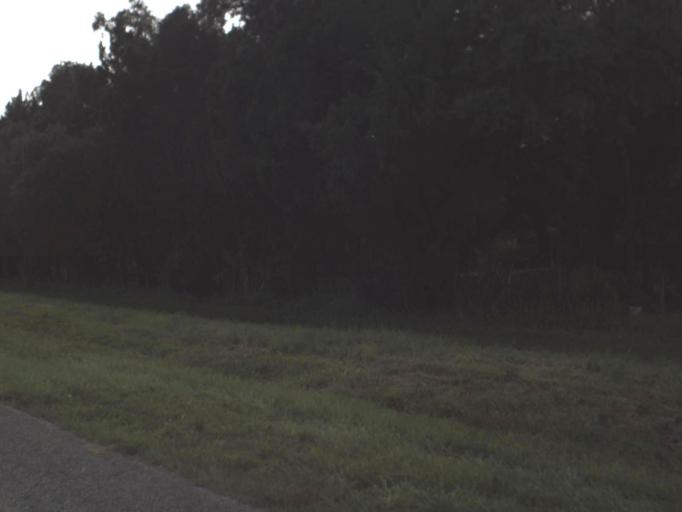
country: US
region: Florida
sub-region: Lee County
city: Alva
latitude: 26.7093
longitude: -81.5718
